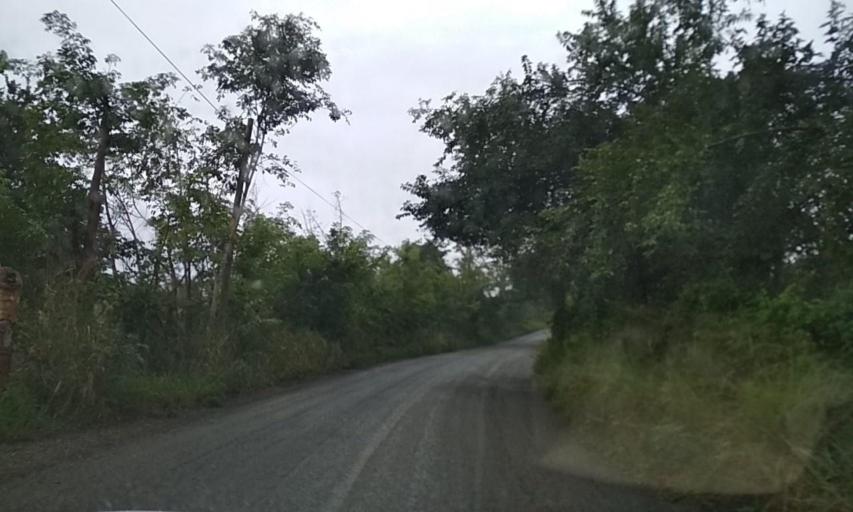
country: MX
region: Veracruz
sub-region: Coatzintla
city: Manuel Maria Contreras
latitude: 20.4572
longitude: -97.4725
